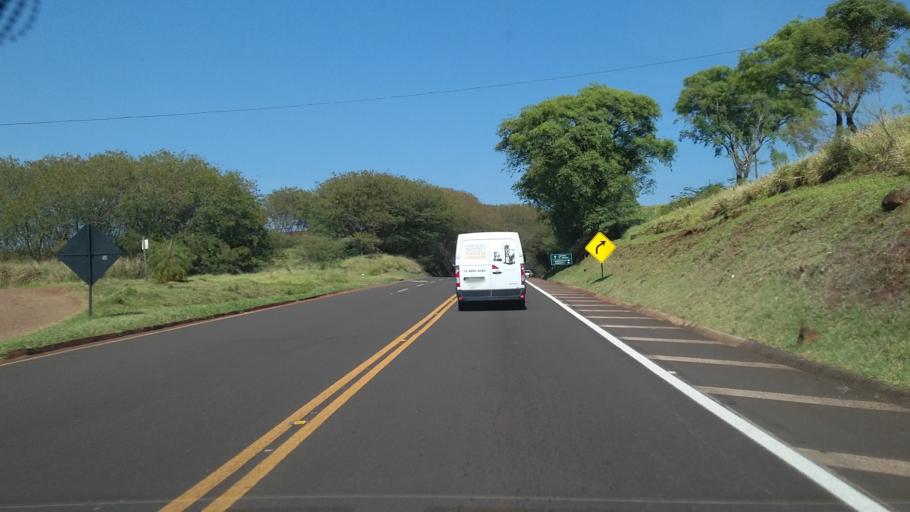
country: BR
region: Parana
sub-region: Bandeirantes
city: Bandeirantes
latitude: -23.1381
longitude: -50.3996
